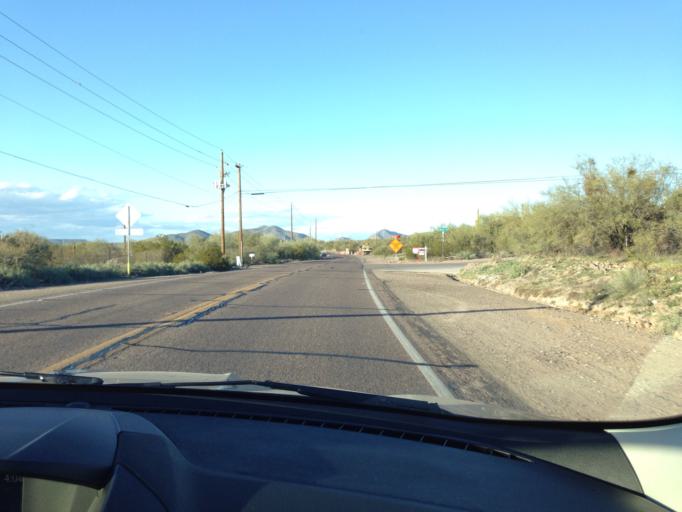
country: US
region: Arizona
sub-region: Maricopa County
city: New River
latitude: 33.8946
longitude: -112.0771
